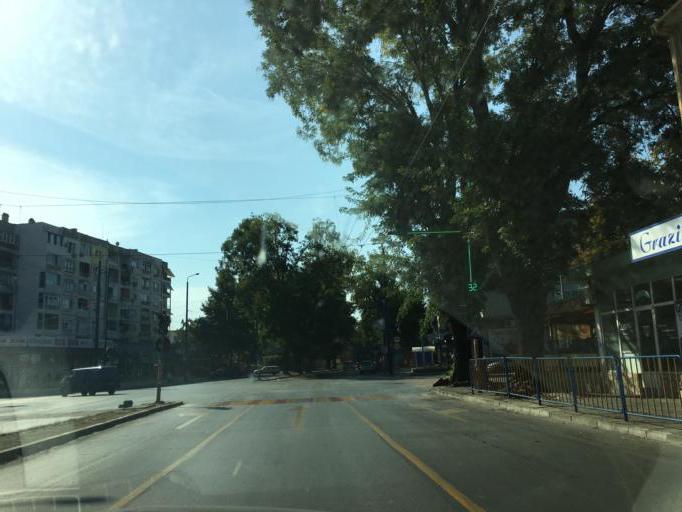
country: BG
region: Pazardzhik
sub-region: Obshtina Pazardzhik
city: Pazardzhik
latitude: 42.1998
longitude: 24.3329
